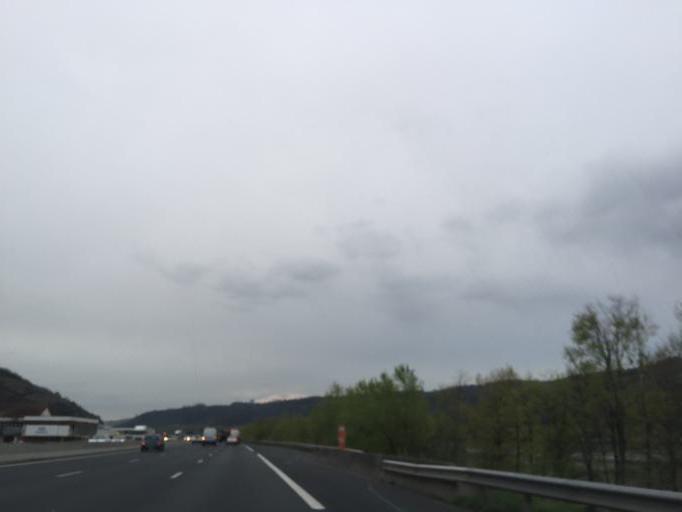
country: FR
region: Rhone-Alpes
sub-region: Departement de l'Isere
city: Seyssuel
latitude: 45.5535
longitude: 4.8277
